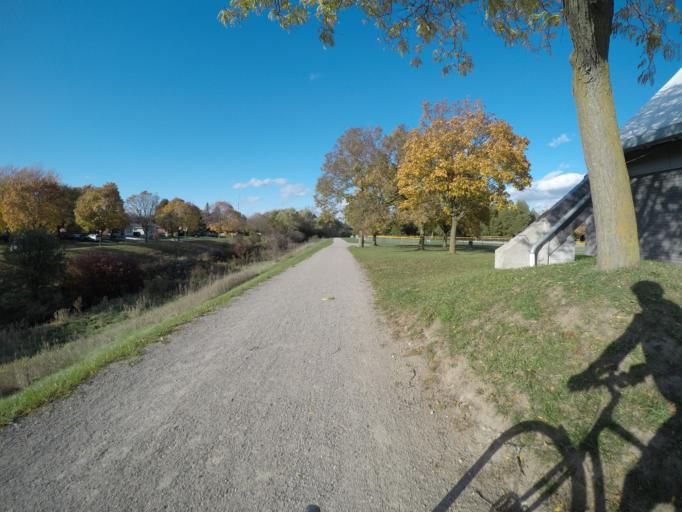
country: CA
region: Ontario
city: Kitchener
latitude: 43.4298
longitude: -80.4592
